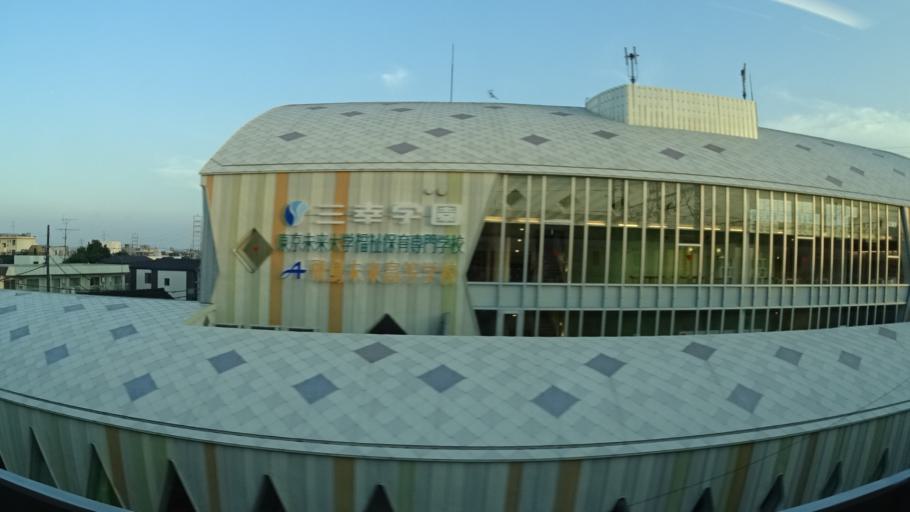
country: JP
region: Saitama
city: Yashio-shi
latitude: 35.7626
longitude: 139.8303
